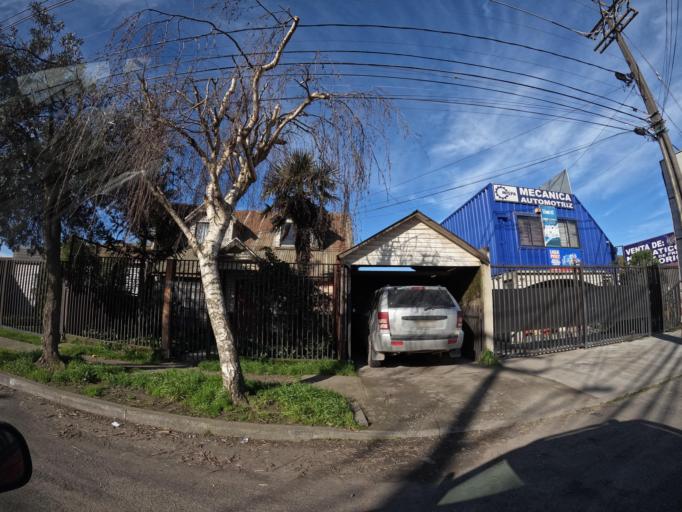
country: CL
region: Biobio
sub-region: Provincia de Concepcion
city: Talcahuano
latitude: -36.7712
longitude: -73.0821
